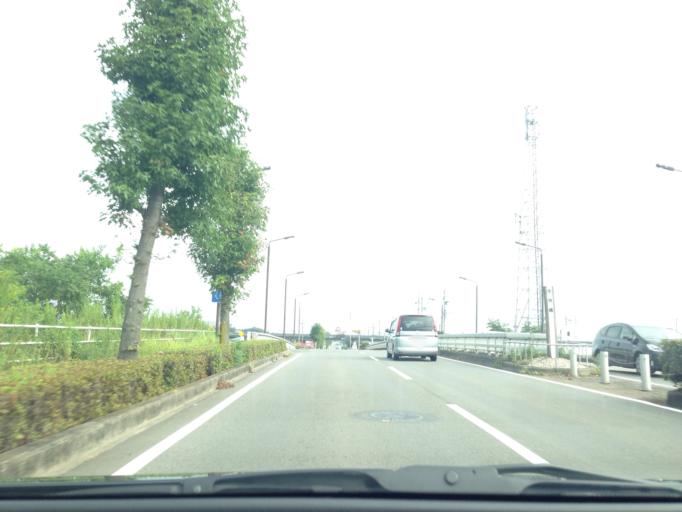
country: JP
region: Aichi
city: Inazawa
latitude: 35.2379
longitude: 136.7793
